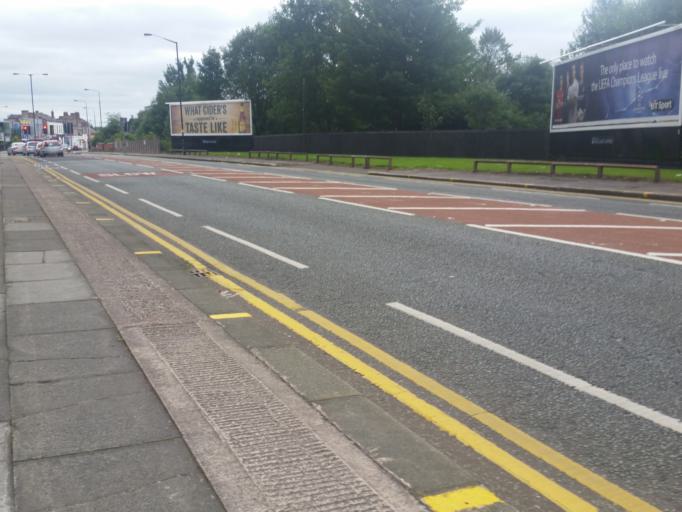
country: GB
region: England
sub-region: Manchester
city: Hulme
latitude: 53.4635
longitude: -2.2722
